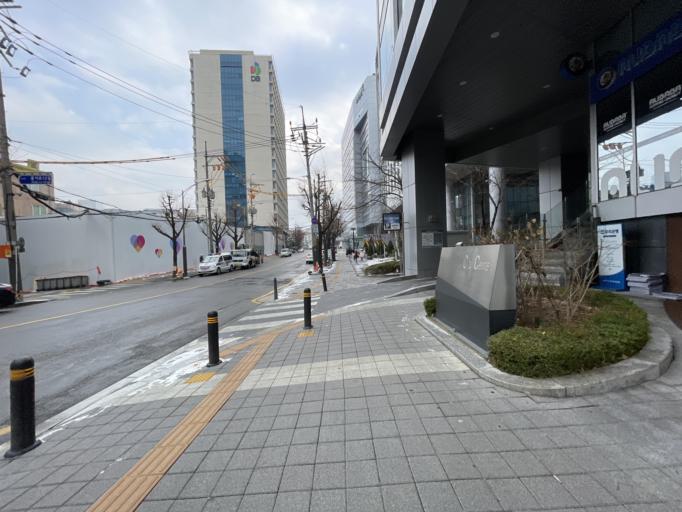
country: KR
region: Seoul
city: Seoul
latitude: 37.5647
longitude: 126.9903
